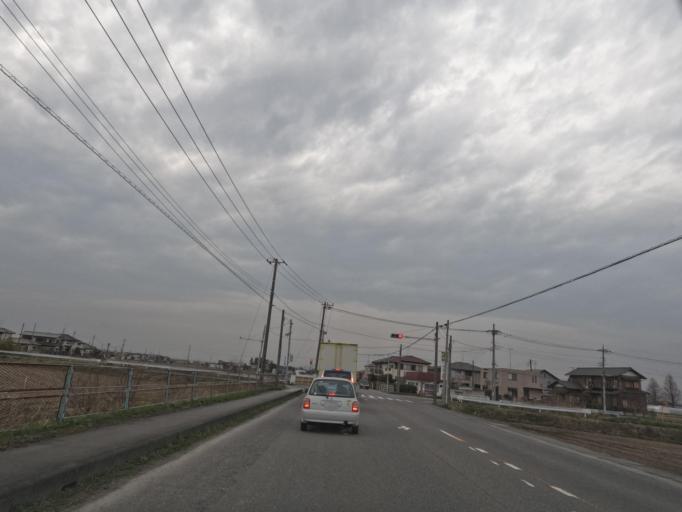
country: JP
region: Ibaraki
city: Toride
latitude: 35.9439
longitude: 140.0602
